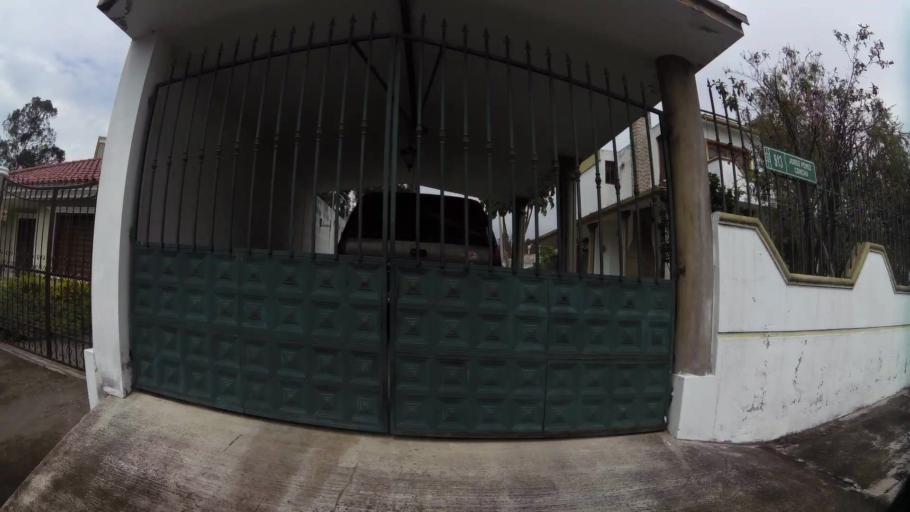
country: EC
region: Pichincha
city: Sangolqui
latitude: -0.3058
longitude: -78.4803
